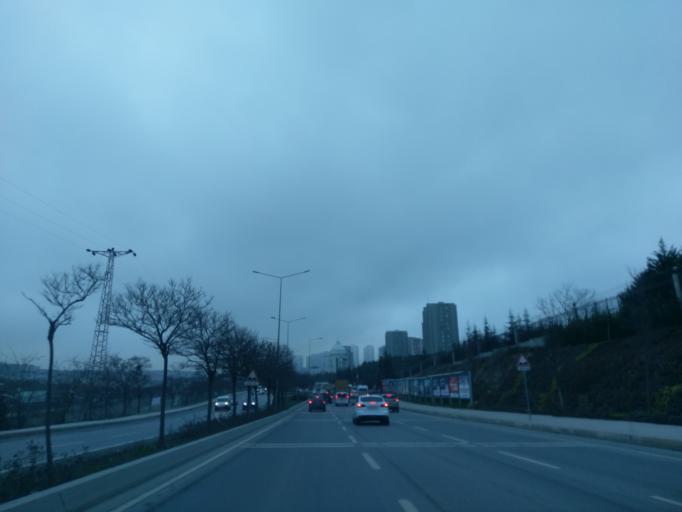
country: TR
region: Istanbul
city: Mahmutbey
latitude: 41.0454
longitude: 28.7740
